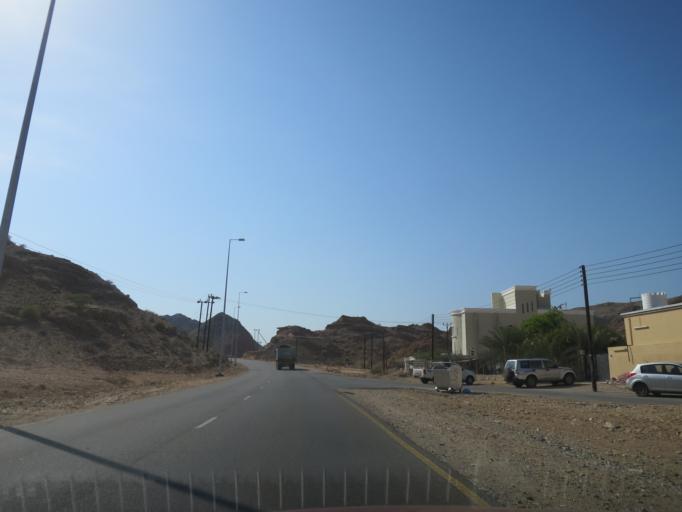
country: OM
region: Muhafazat Masqat
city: Muscat
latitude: 23.5160
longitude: 58.7146
